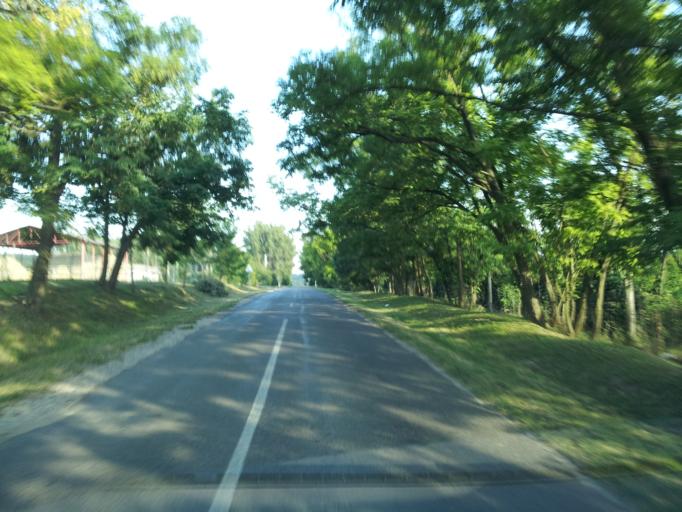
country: HU
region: Fejer
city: Many
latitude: 47.5322
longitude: 18.5941
